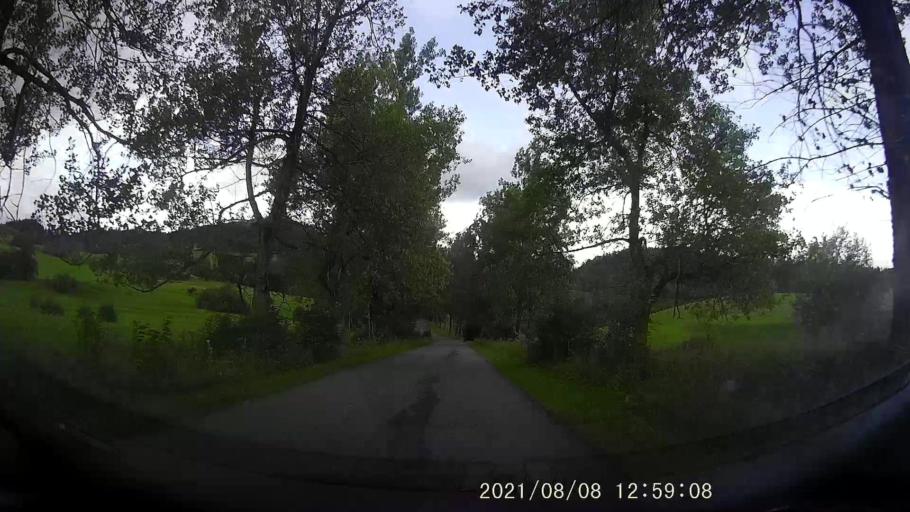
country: PL
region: Lower Silesian Voivodeship
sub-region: Powiat klodzki
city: Duszniki-Zdroj
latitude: 50.4092
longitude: 16.3526
